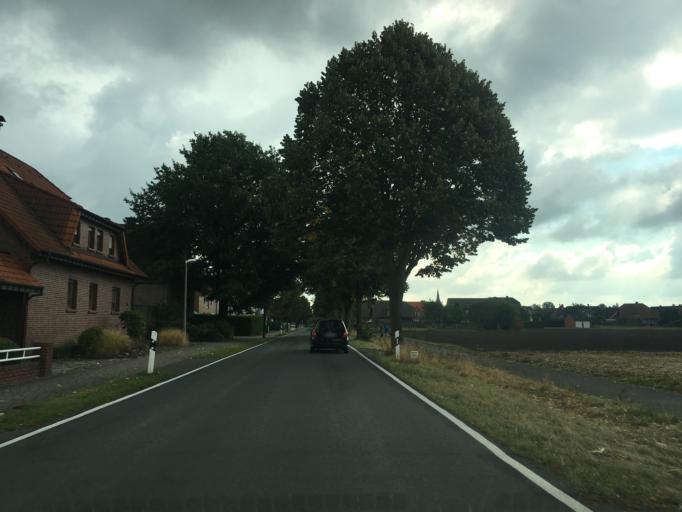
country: DE
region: North Rhine-Westphalia
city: Olfen
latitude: 51.7129
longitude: 7.3687
